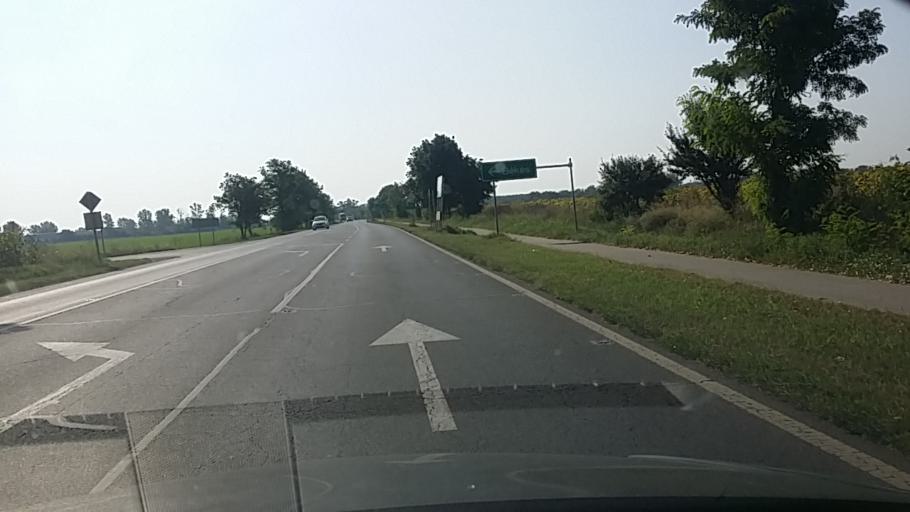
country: HU
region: Bekes
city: Kondoros
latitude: 46.7379
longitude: 20.8896
